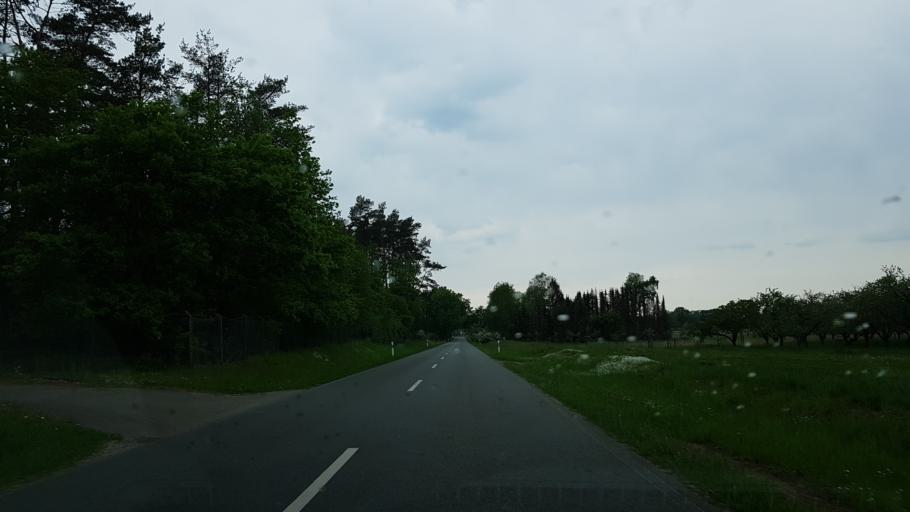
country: DE
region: Lower Saxony
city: Gorleben
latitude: 53.0634
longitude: 11.4152
